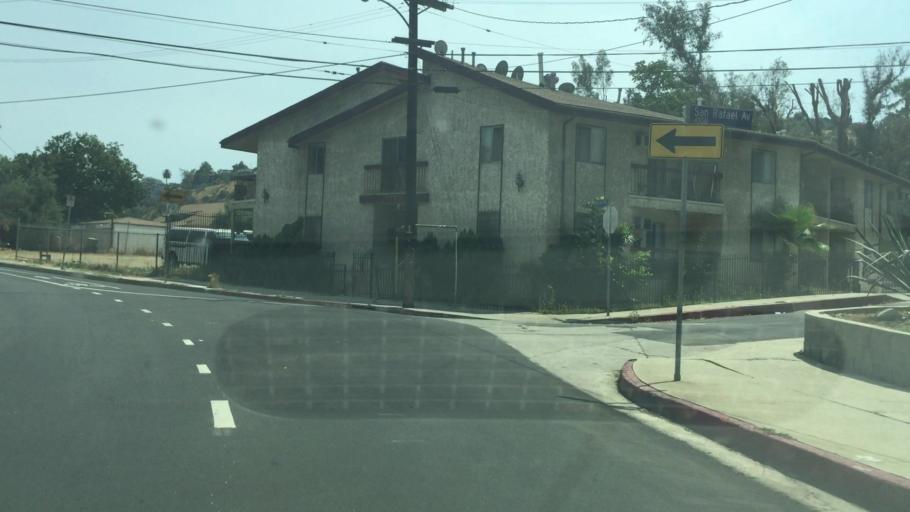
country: US
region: California
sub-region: Los Angeles County
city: Glendale
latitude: 34.1128
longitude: -118.2081
